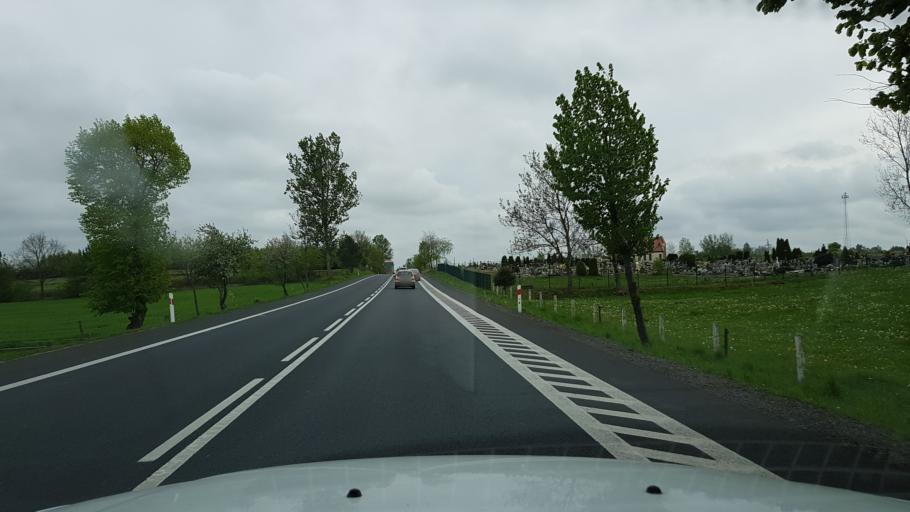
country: PL
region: West Pomeranian Voivodeship
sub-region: Powiat slawienski
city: Darlowo
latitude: 54.3046
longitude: 16.5107
